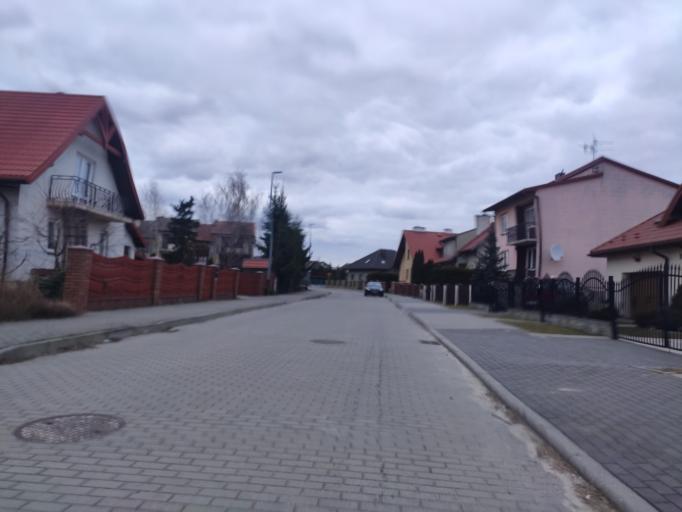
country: PL
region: Lublin Voivodeship
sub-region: Powiat lubartowski
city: Kock
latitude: 51.6396
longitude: 22.4322
